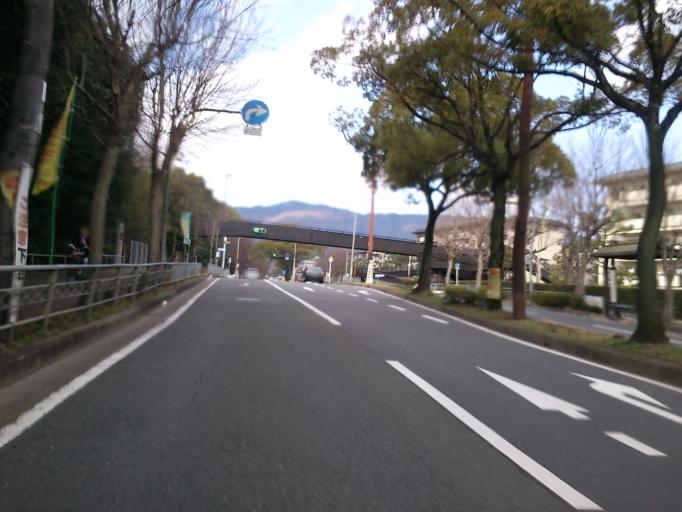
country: JP
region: Kyoto
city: Muko
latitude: 34.9551
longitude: 135.6814
